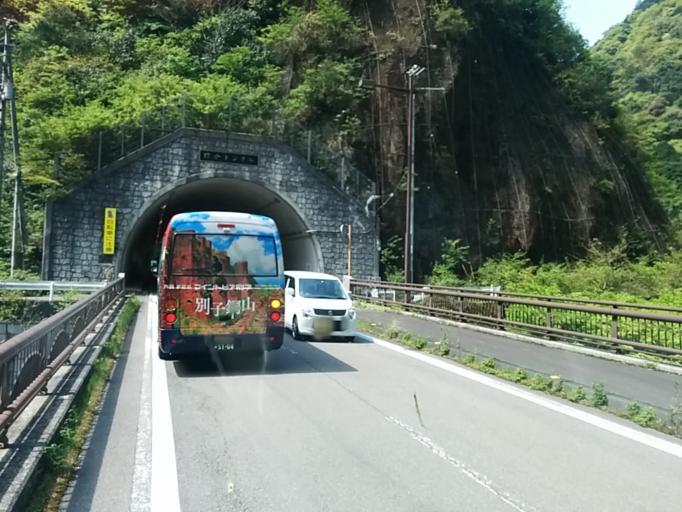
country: JP
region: Ehime
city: Niihama
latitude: 33.8863
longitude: 133.3051
